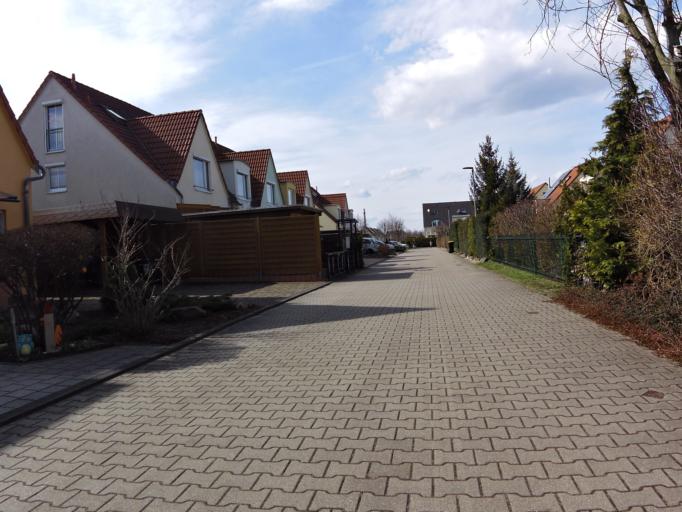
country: DE
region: Saxony
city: Taucha
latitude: 51.3383
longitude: 12.4845
